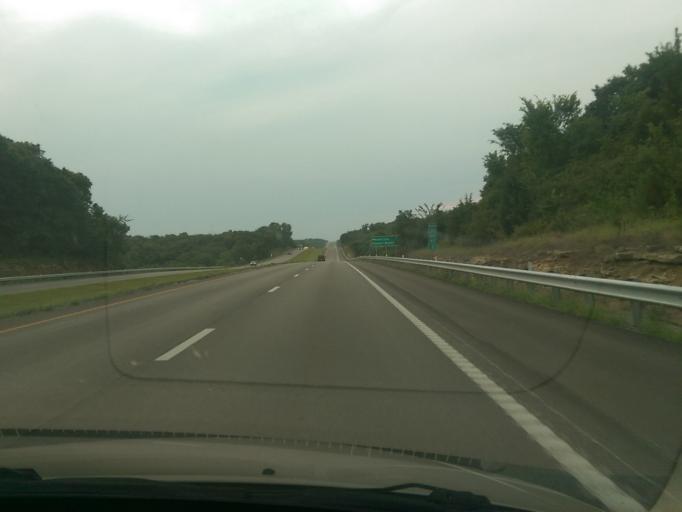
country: US
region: Missouri
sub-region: Andrew County
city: Savannah
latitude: 39.9267
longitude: -94.9184
